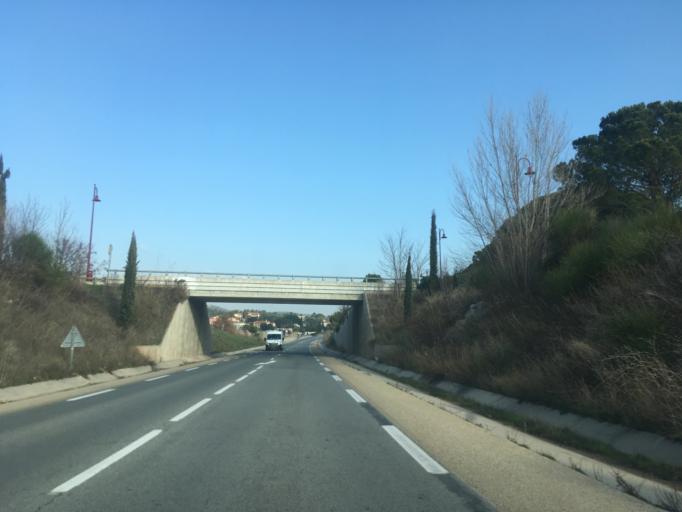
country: FR
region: Provence-Alpes-Cote d'Azur
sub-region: Departement du Var
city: Vidauban
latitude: 43.4274
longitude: 6.4353
